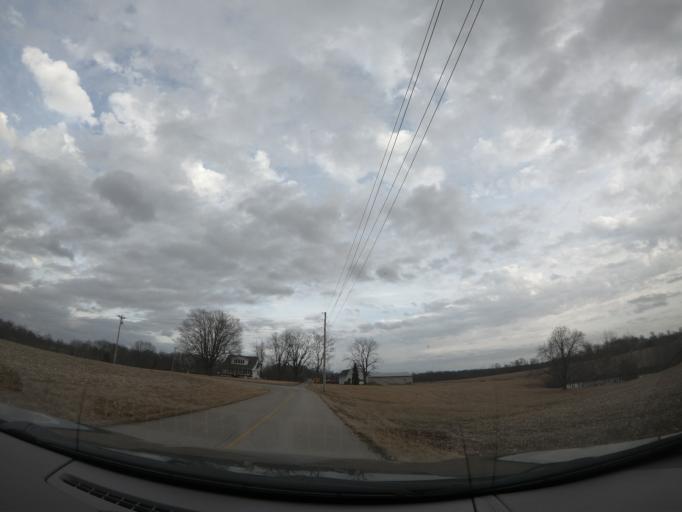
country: US
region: Indiana
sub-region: Floyd County
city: Galena
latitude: 38.3785
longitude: -85.9114
